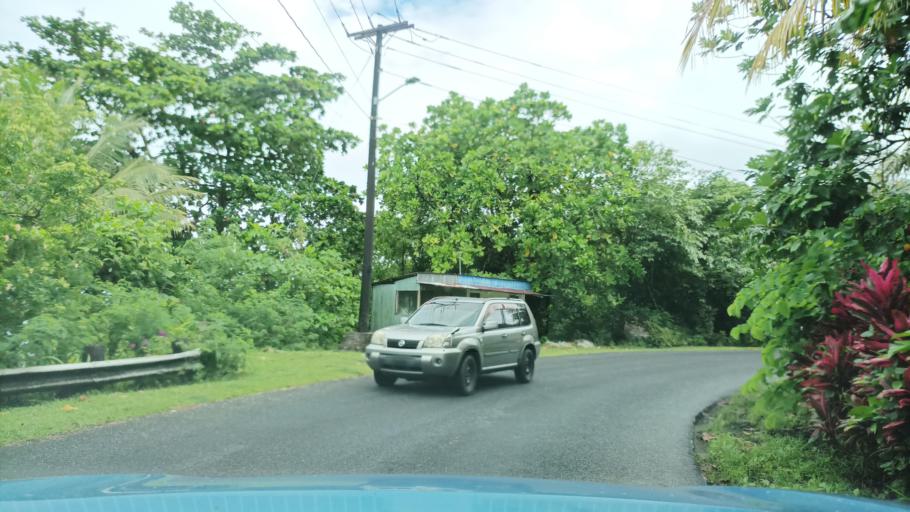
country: FM
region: Pohnpei
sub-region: Kolonia Municipality
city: Kolonia
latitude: 6.9620
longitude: 158.2492
